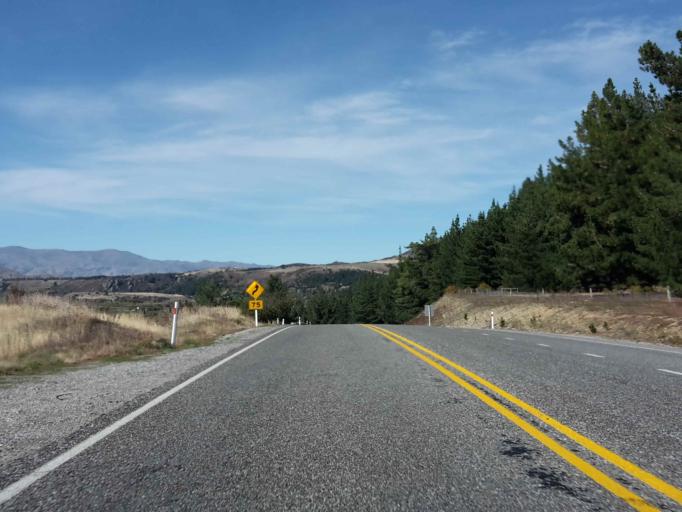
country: NZ
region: Otago
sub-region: Queenstown-Lakes District
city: Wanaka
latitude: -44.7294
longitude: 169.2528
